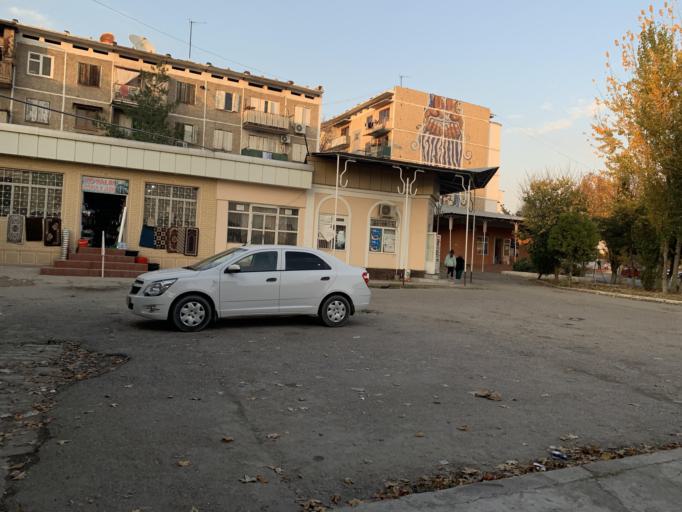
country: UZ
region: Namangan
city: Namangan Shahri
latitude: 41.0051
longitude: 71.5993
